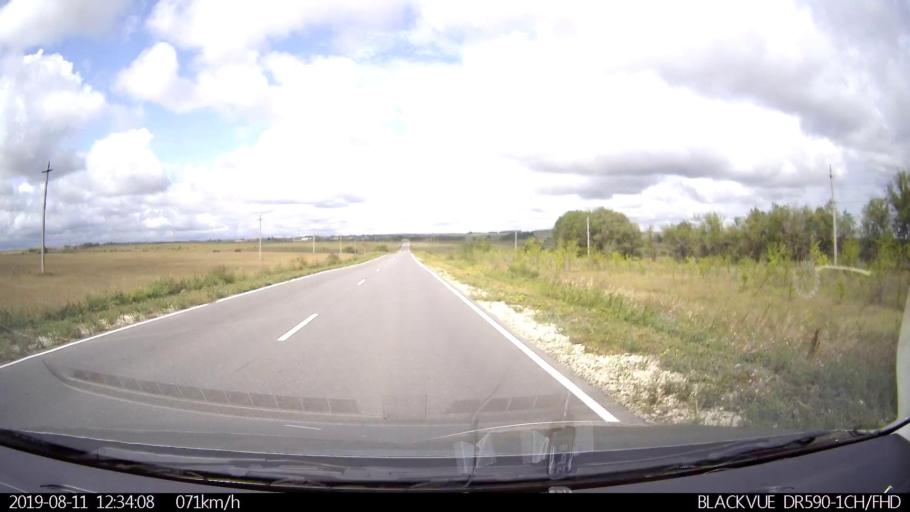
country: RU
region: Ulyanovsk
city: Ignatovka
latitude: 53.8146
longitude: 47.8468
